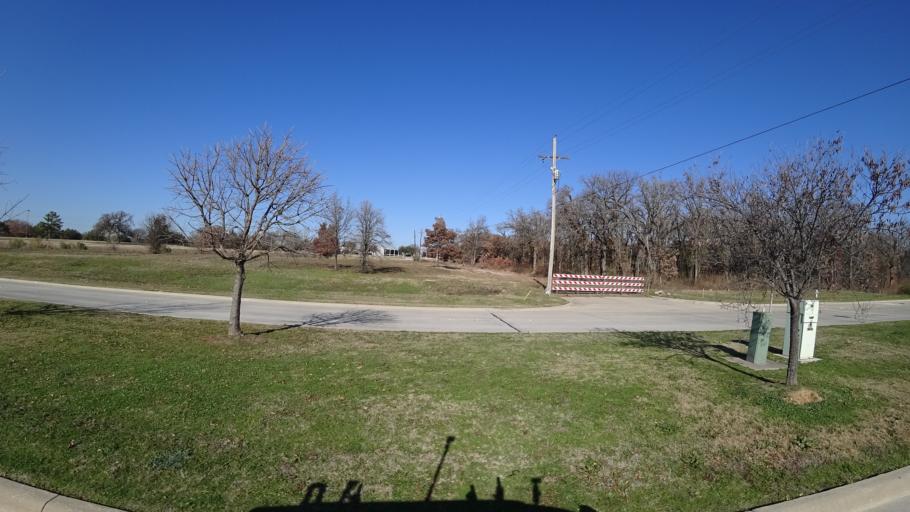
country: US
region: Texas
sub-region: Dallas County
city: Coppell
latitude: 32.9941
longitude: -97.0024
